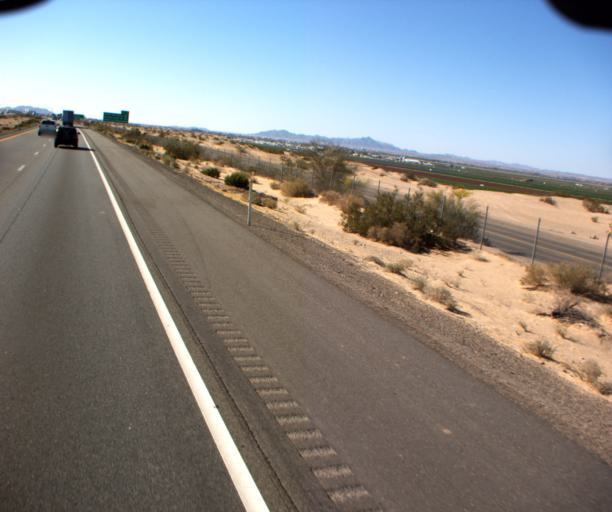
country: US
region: Arizona
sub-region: Yuma County
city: Yuma
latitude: 32.6853
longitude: -114.5648
